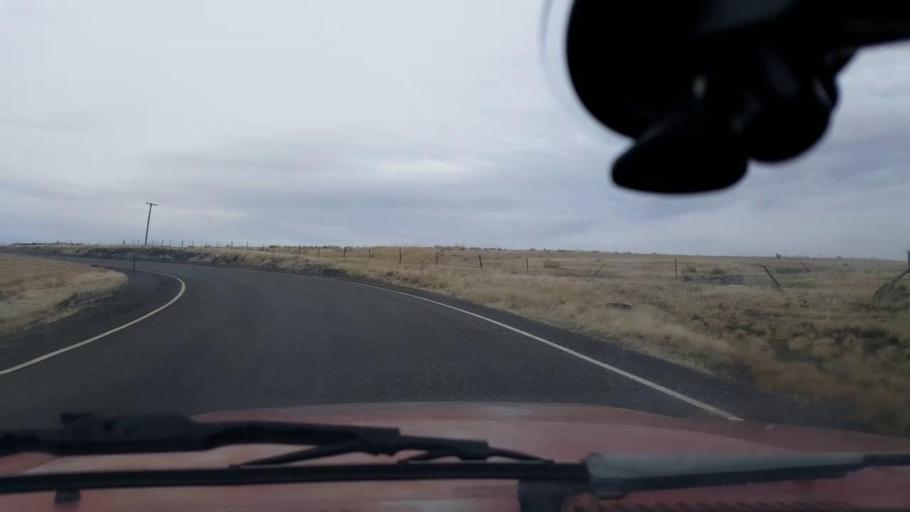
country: US
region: Washington
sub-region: Asotin County
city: Clarkston Heights-Vineland
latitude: 46.3231
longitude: -117.3536
